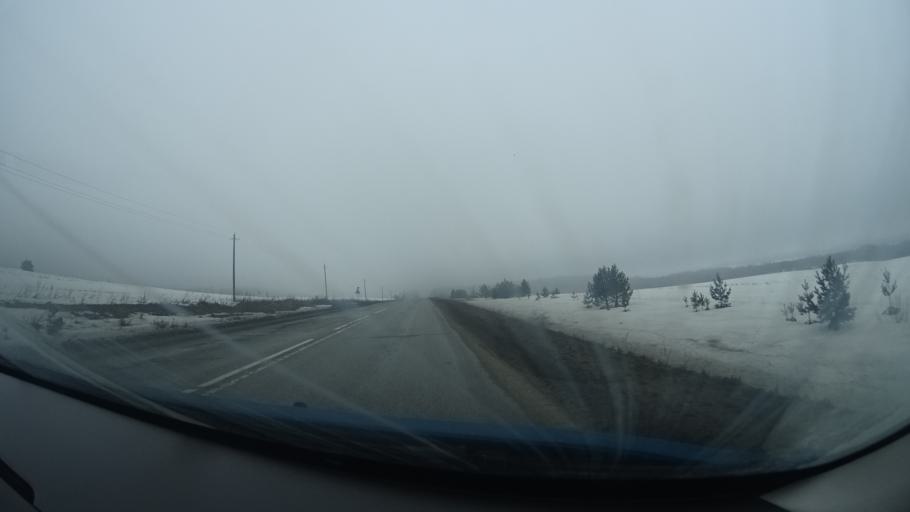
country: RU
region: Perm
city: Kuyeda
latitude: 56.4713
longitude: 55.7436
